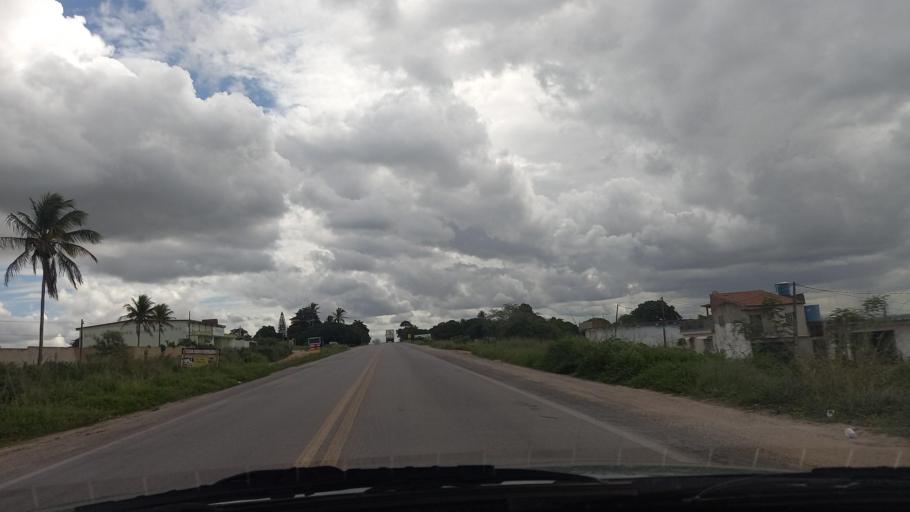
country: BR
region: Pernambuco
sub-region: Lajedo
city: Lajedo
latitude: -8.6598
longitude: -36.3366
